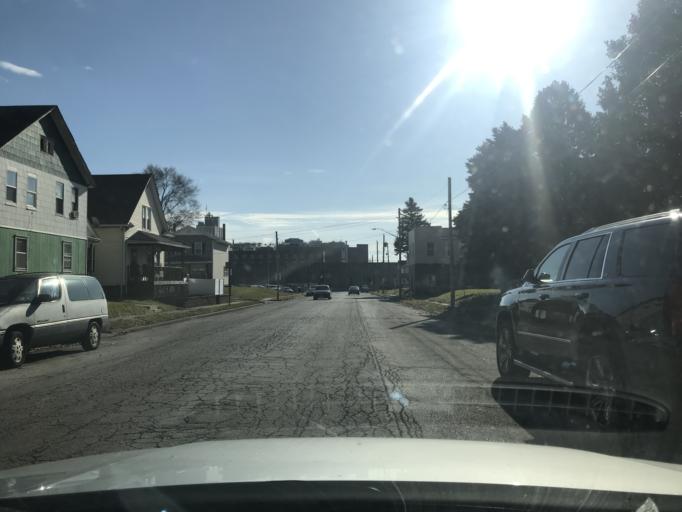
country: US
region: Illinois
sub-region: Rock Island County
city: Rock Island
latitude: 41.5182
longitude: -90.6085
